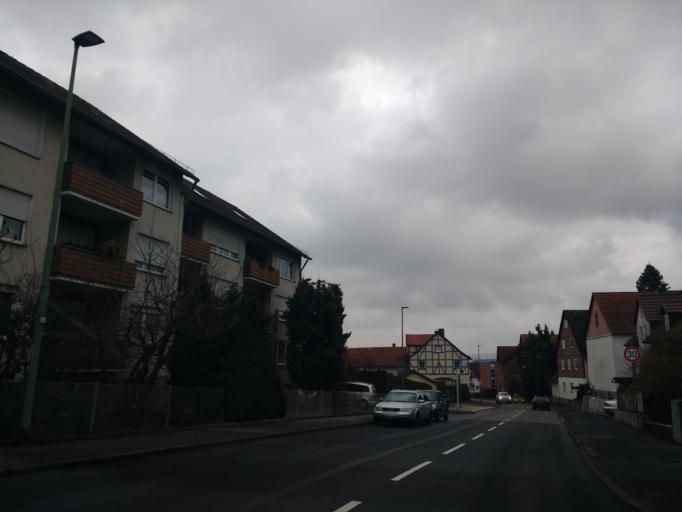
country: DE
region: Hesse
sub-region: Regierungsbezirk Kassel
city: Baunatal
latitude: 51.2805
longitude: 9.4269
